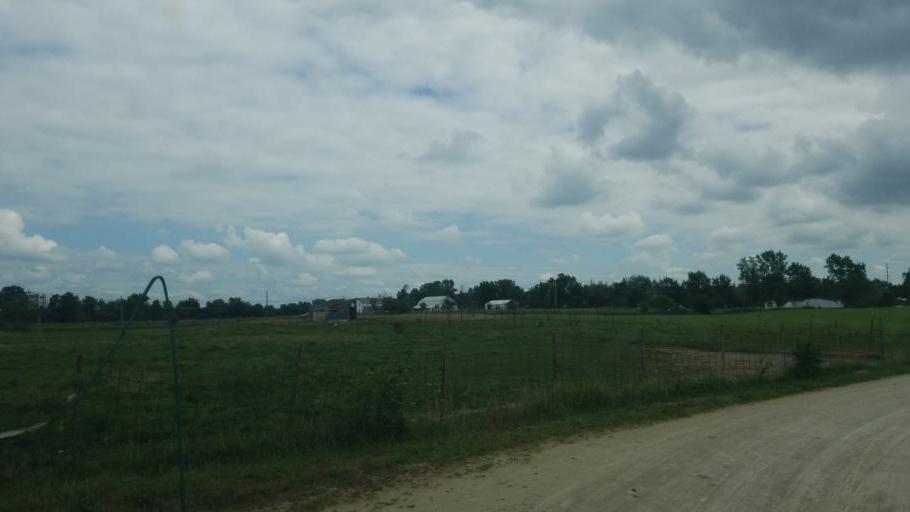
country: US
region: Indiana
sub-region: Adams County
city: Geneva
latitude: 40.6239
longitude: -84.9568
